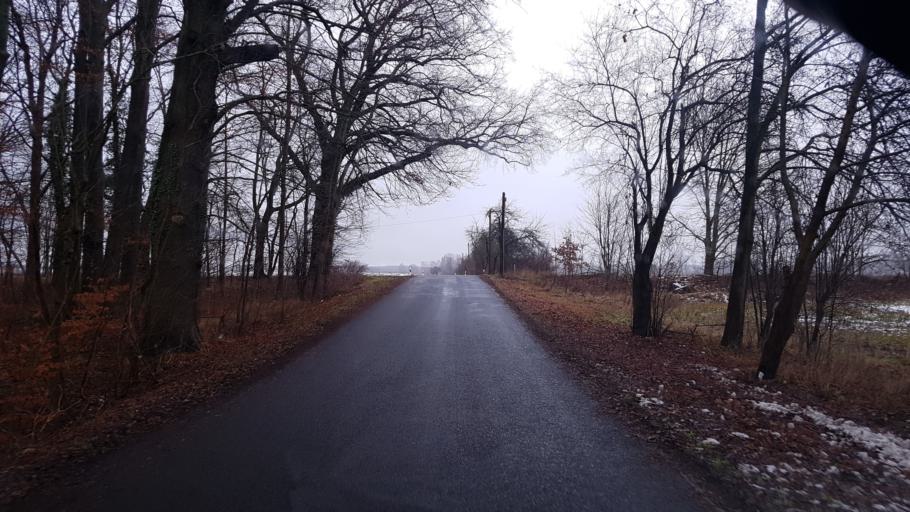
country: DE
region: Brandenburg
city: Lieberose
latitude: 51.9810
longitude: 14.3139
